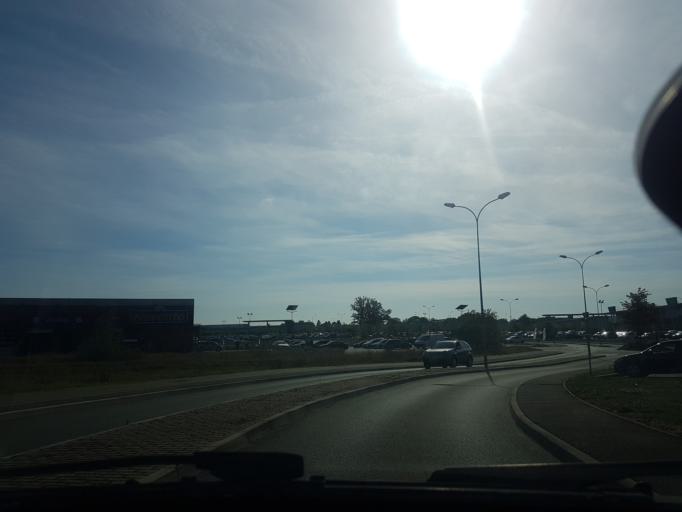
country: FR
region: Franche-Comte
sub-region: Territoire de Belfort
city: Chevremont
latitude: 47.6439
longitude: 6.9214
